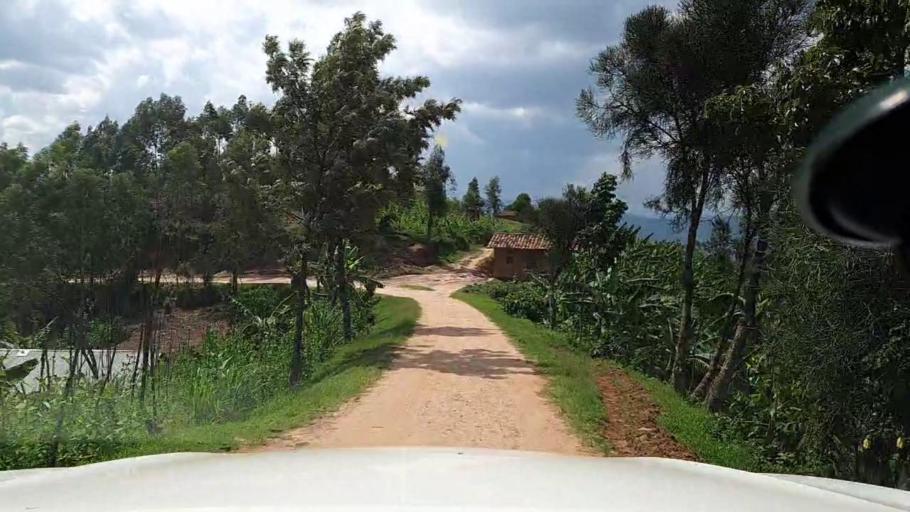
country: RW
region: Southern Province
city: Gitarama
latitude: -1.8400
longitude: 29.8167
